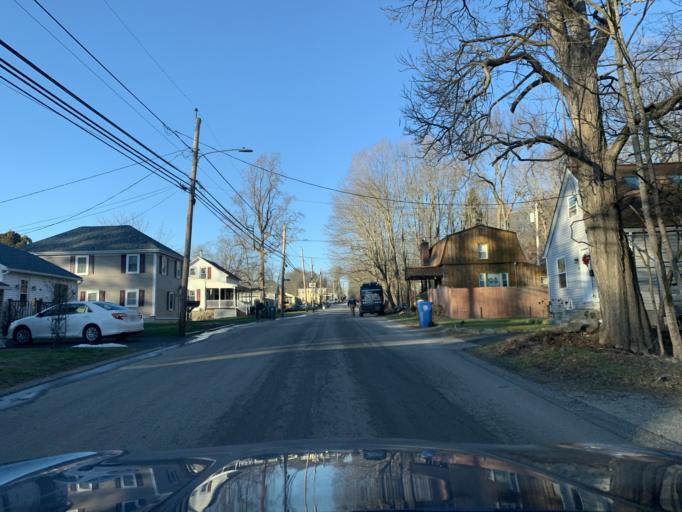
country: US
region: Rhode Island
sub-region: Kent County
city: West Warwick
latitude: 41.7367
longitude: -71.5487
